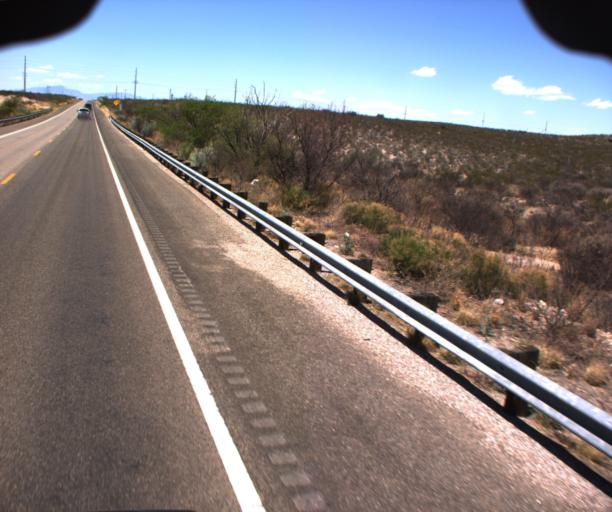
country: US
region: Arizona
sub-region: Cochise County
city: Tombstone
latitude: 31.7421
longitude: -110.0903
